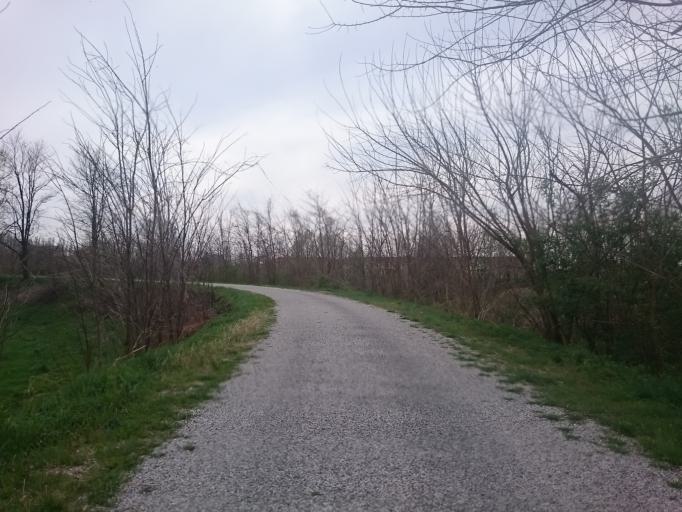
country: IT
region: Veneto
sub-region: Provincia di Padova
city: Limena
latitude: 45.4731
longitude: 11.8503
